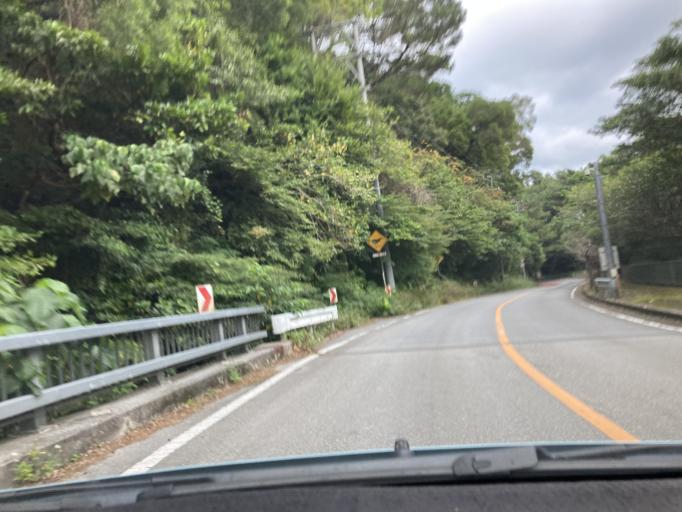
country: JP
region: Okinawa
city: Nago
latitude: 26.8308
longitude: 128.2771
